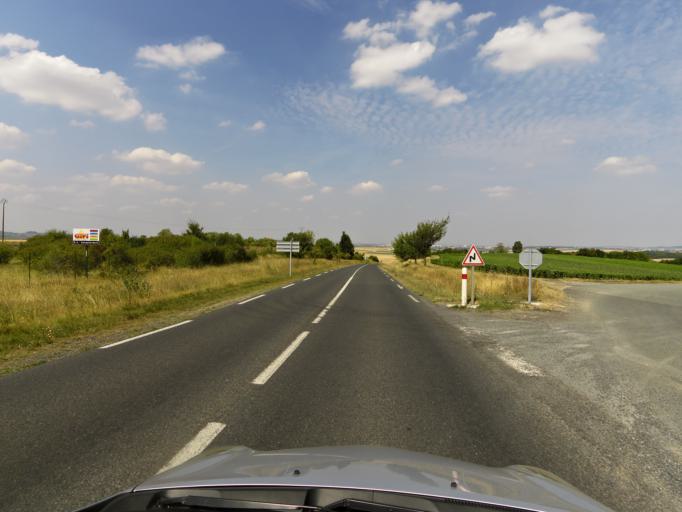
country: FR
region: Champagne-Ardenne
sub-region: Departement de la Marne
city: Rilly-la-Montagne
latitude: 49.1685
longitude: 4.0115
